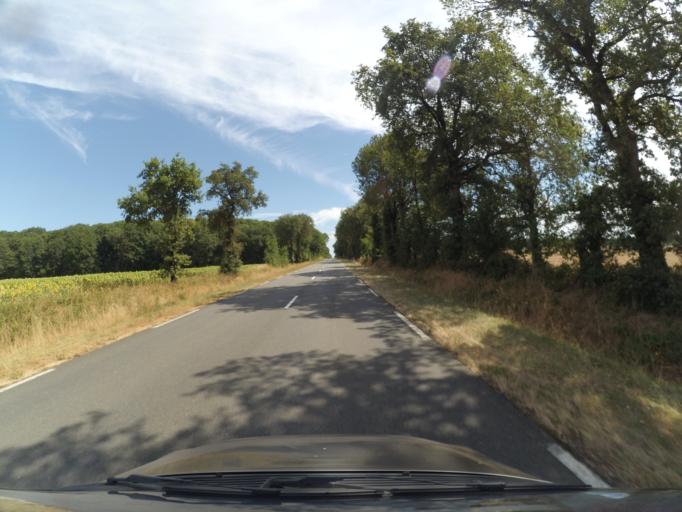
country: FR
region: Poitou-Charentes
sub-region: Departement de la Charente
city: Confolens
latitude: 46.0540
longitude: 0.6134
